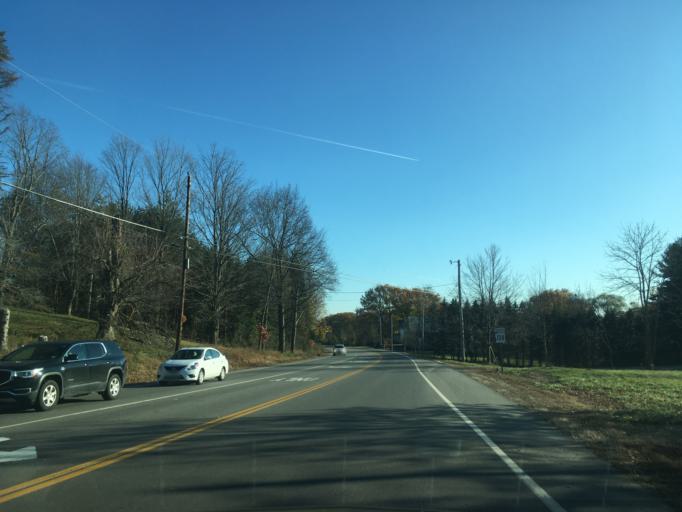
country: US
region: New Hampshire
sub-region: Rockingham County
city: Stratham Station
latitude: 43.0425
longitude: -70.9308
